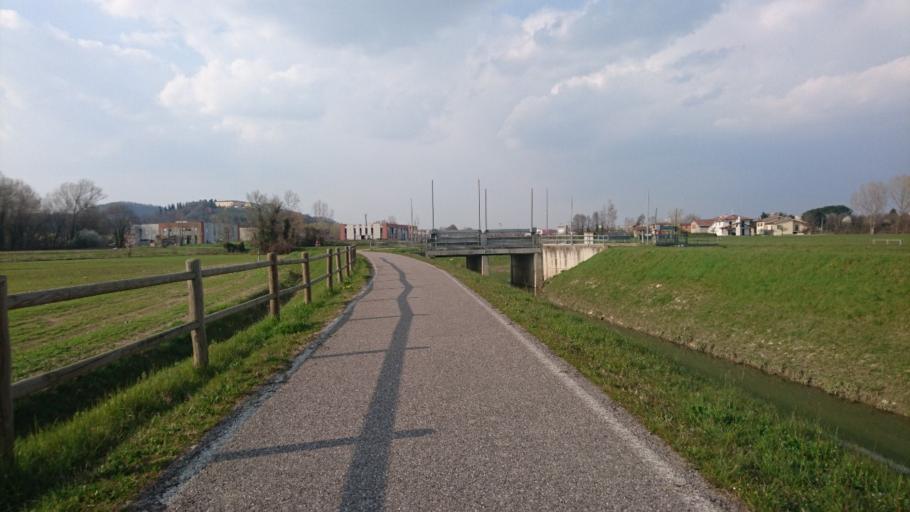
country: IT
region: Veneto
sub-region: Provincia di Padova
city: Montegrotto Terme
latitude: 45.3357
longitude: 11.7734
